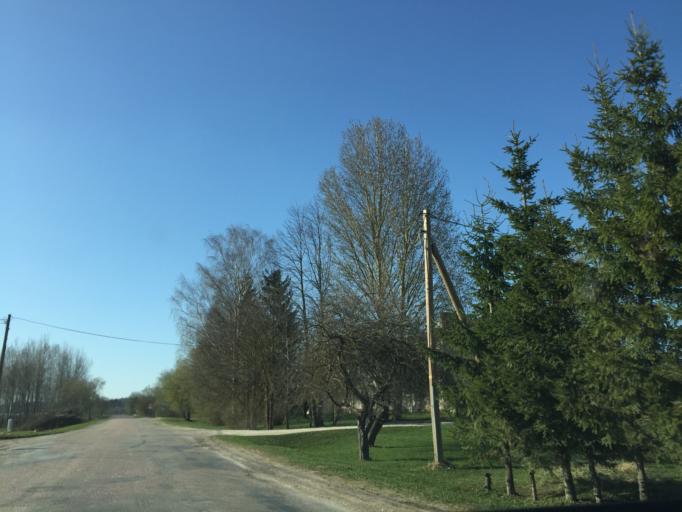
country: LV
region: Ropazu
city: Ropazi
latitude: 56.9619
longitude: 24.6881
